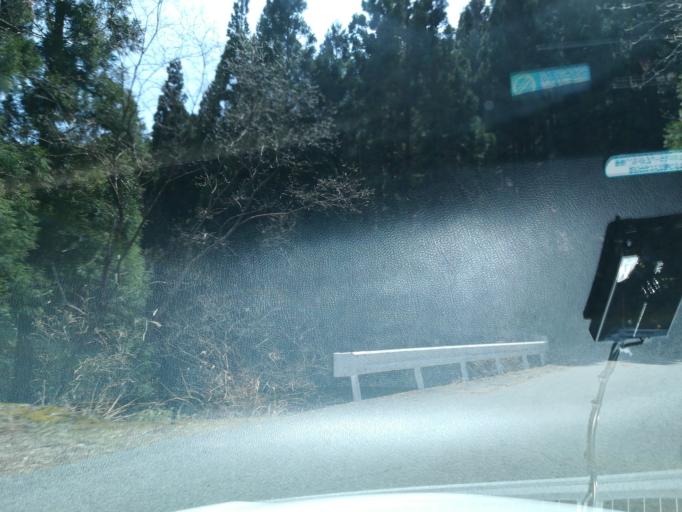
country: JP
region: Tokushima
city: Wakimachi
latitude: 33.8790
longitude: 134.0514
